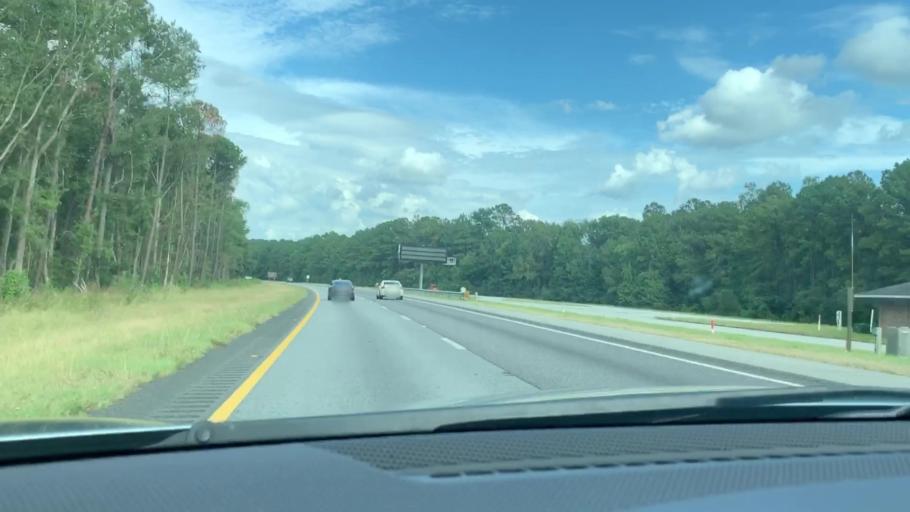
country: US
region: South Carolina
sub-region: Jasper County
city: Hardeeville
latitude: 32.2560
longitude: -81.1005
